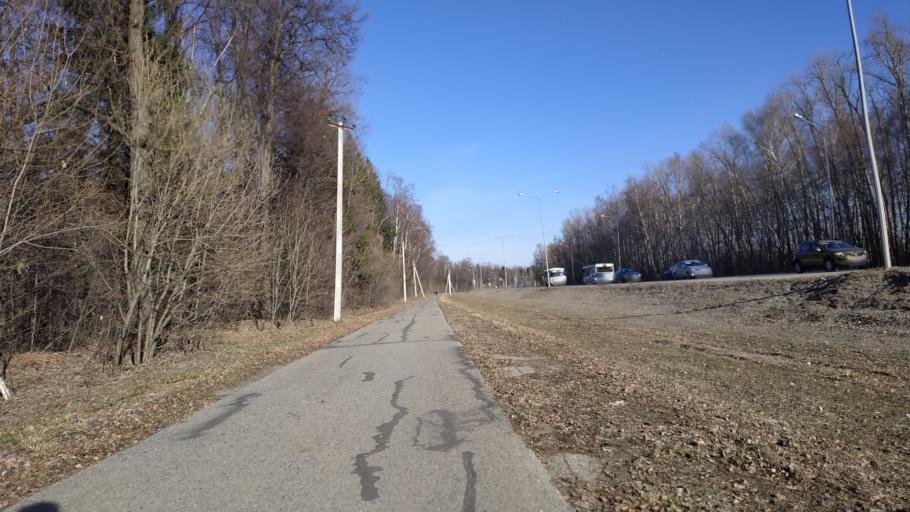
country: RU
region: Chuvashia
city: Ishley
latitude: 56.1336
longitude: 47.1044
